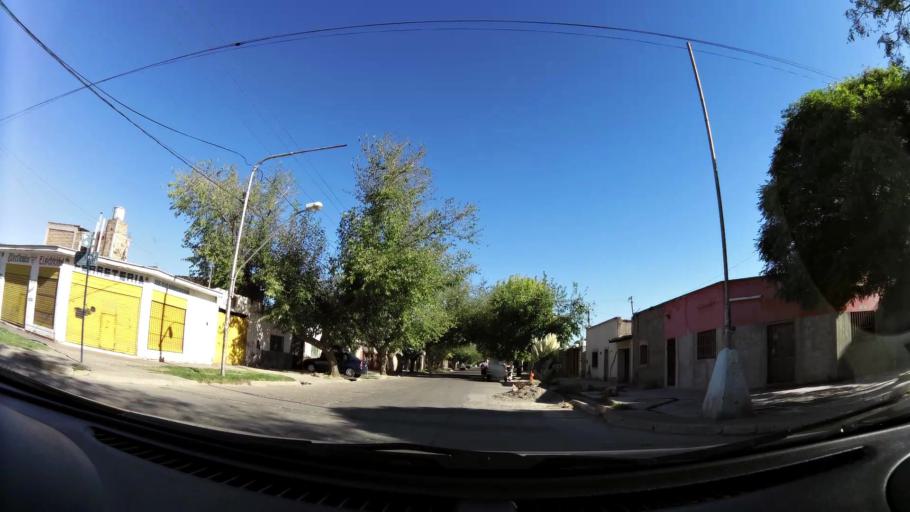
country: AR
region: Mendoza
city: Las Heras
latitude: -32.8541
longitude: -68.8292
